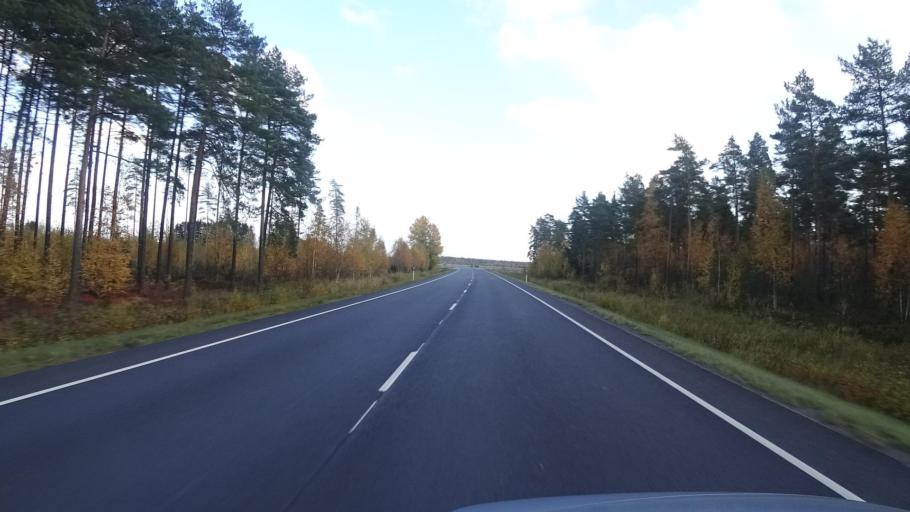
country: FI
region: Satakunta
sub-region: Rauma
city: Koeylioe
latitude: 61.0792
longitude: 22.2794
